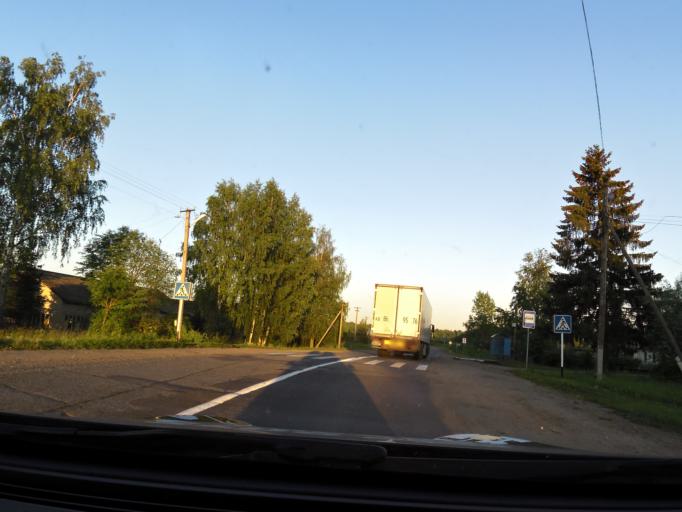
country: RU
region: Jaroslavl
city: Prechistoye
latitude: 58.4087
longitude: 40.3712
